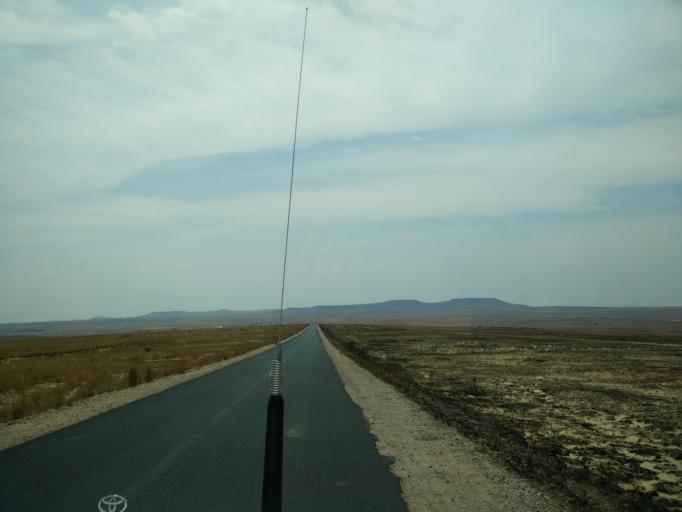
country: MG
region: Ihorombe
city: Ranohira
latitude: -22.7791
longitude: 45.0812
